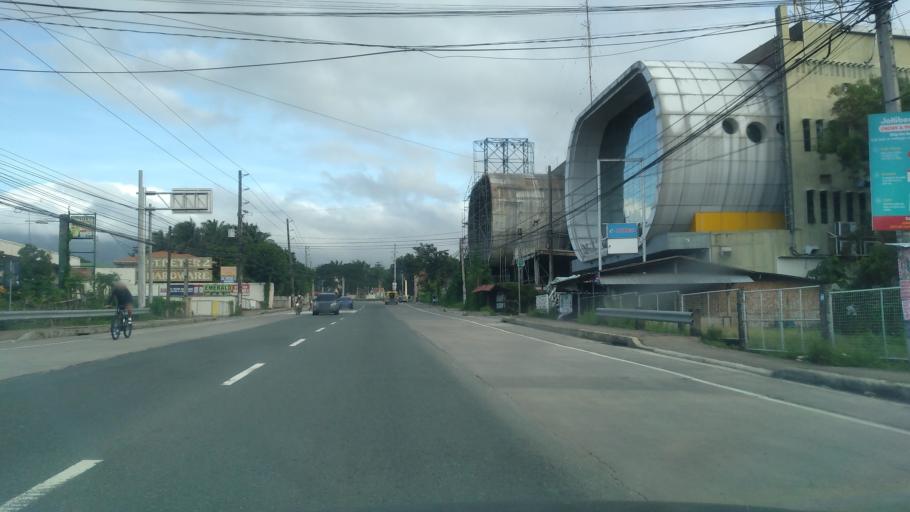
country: PH
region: Calabarzon
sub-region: Province of Quezon
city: Isabang
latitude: 13.9661
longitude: 121.5640
